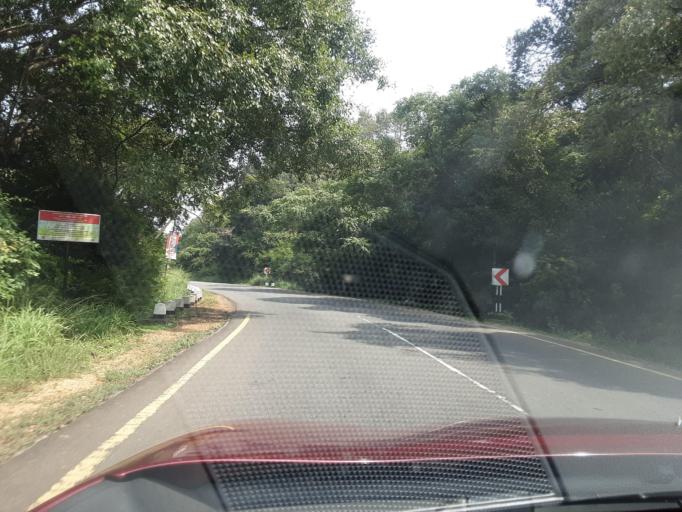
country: LK
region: North Central
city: Anuradhapura
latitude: 8.3466
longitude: 80.5064
